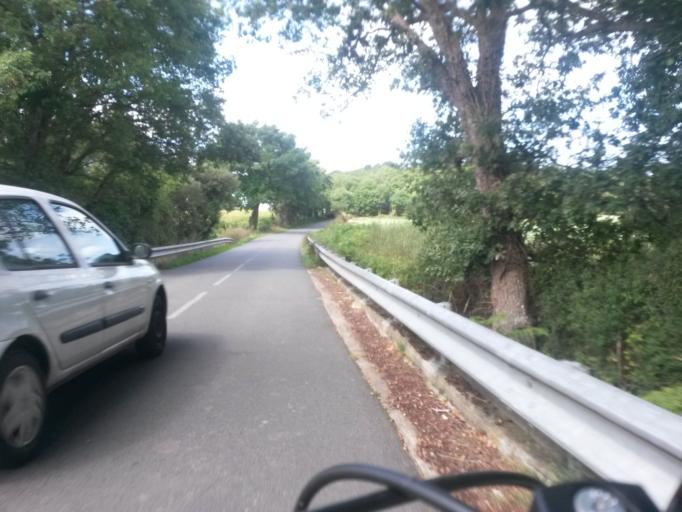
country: FR
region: Pays de la Loire
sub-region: Departement de la Loire-Atlantique
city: Asserac
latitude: 47.3902
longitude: -2.3597
